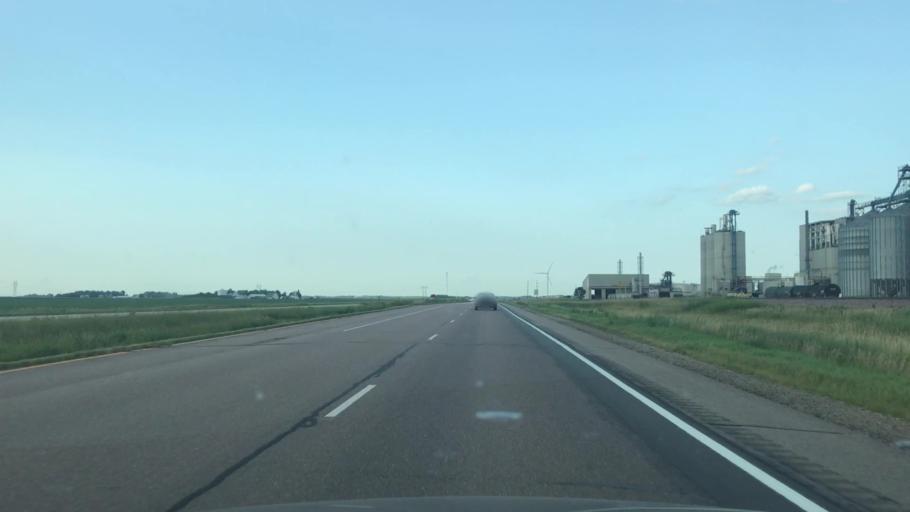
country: US
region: Minnesota
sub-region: Nobles County
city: Worthington
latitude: 43.7037
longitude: -95.4636
